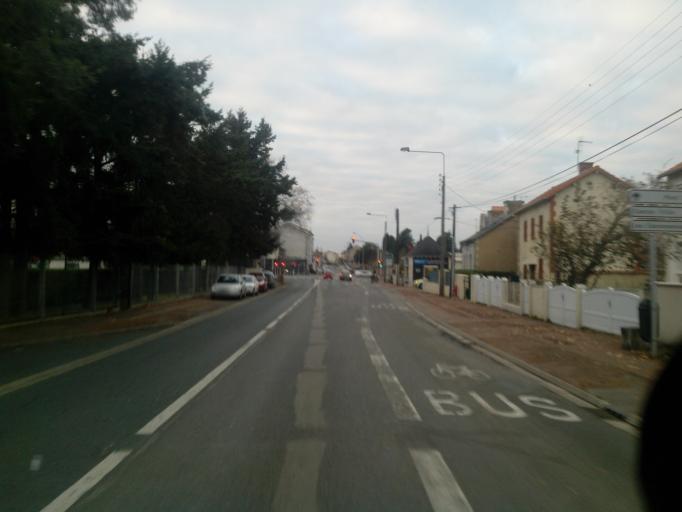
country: FR
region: Poitou-Charentes
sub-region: Departement de la Vienne
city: Saint-Benoit
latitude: 46.5717
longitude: 0.3722
